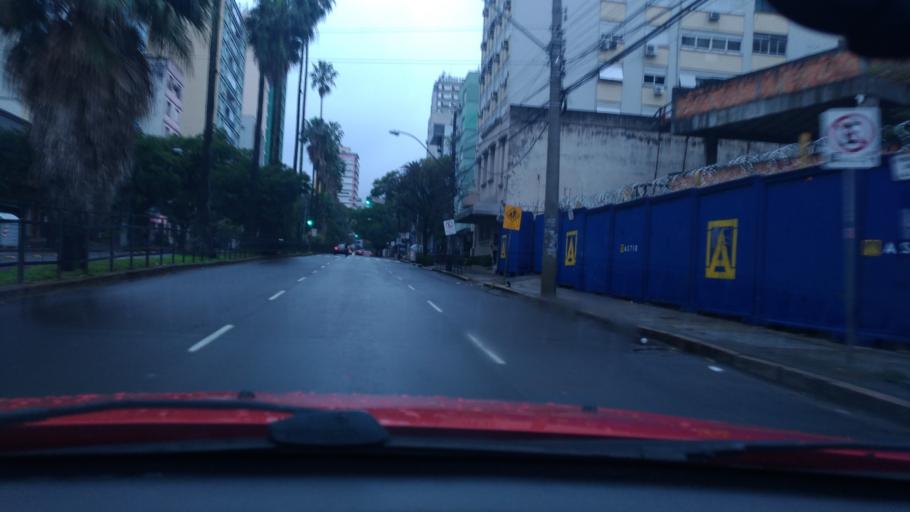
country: BR
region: Rio Grande do Sul
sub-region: Porto Alegre
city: Porto Alegre
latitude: -30.0293
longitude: -51.2108
